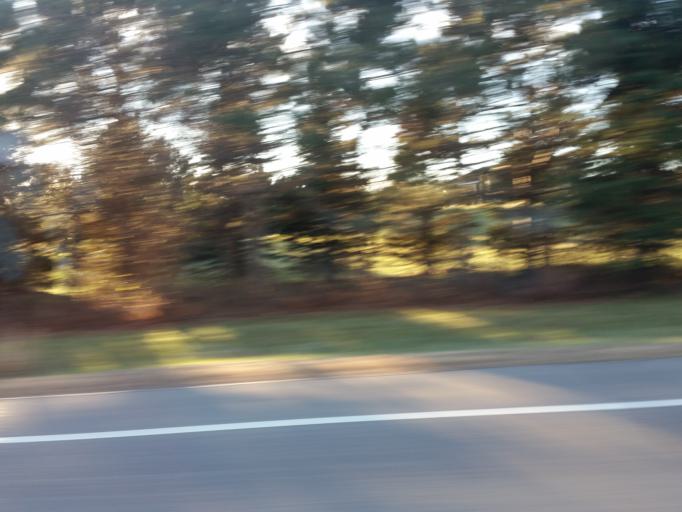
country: US
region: Minnesota
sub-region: Washington County
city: Stillwater
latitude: 45.0840
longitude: -92.8326
